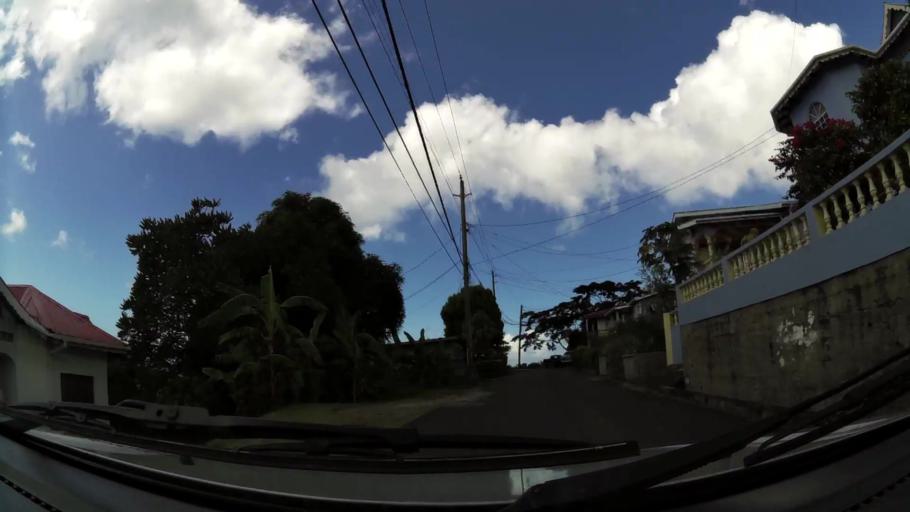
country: GD
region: Saint Mark
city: Victoria
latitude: 12.1823
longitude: -61.7236
